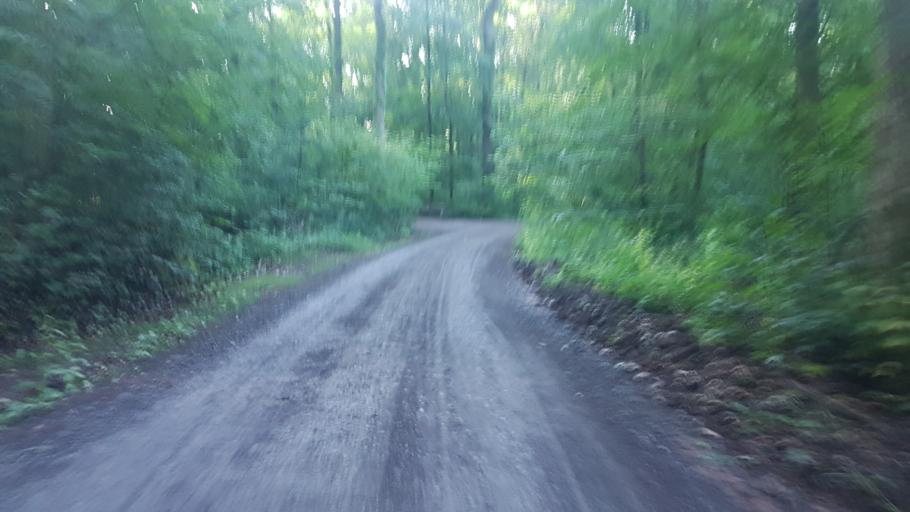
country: DE
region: Baden-Wuerttemberg
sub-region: Karlsruhe Region
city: Sternenfels
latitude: 49.0519
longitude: 8.8805
